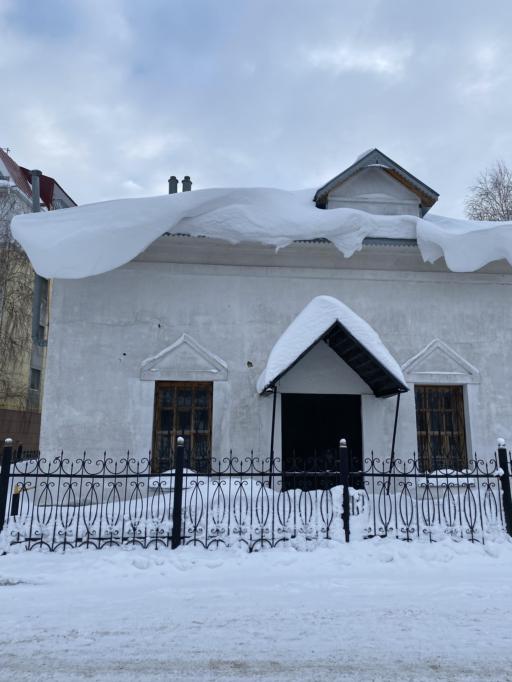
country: RU
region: Tjumen
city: Tobol'sk
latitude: 58.2021
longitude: 68.2527
